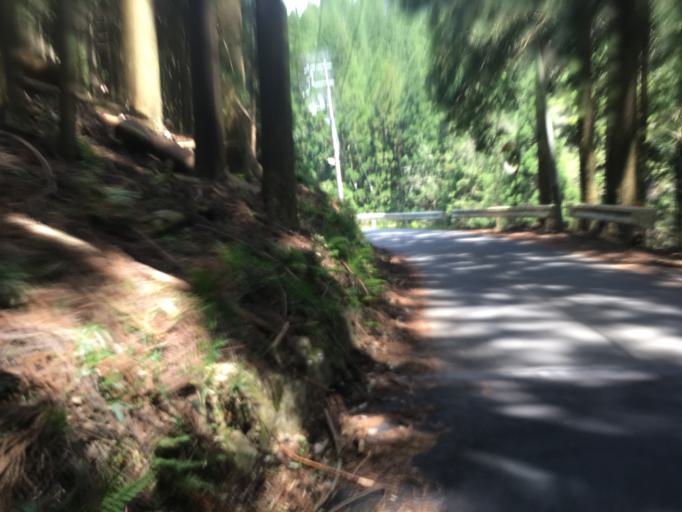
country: JP
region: Kyoto
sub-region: Kyoto-shi
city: Kamigyo-ku
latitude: 35.1069
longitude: 135.7339
